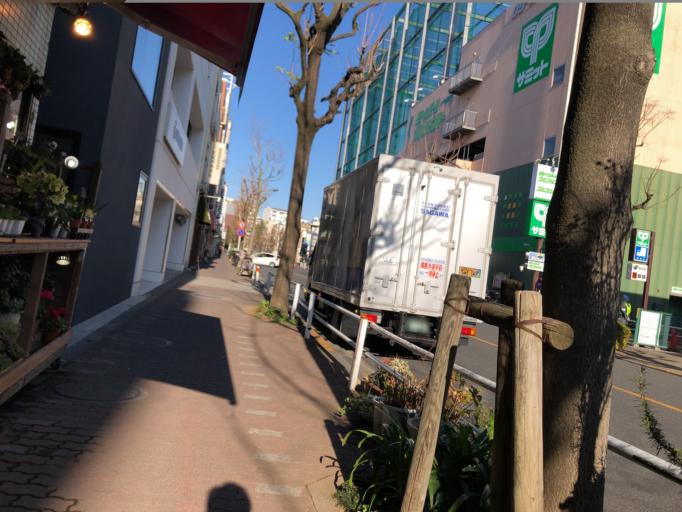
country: JP
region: Tokyo
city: Musashino
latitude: 35.7136
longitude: 139.5617
